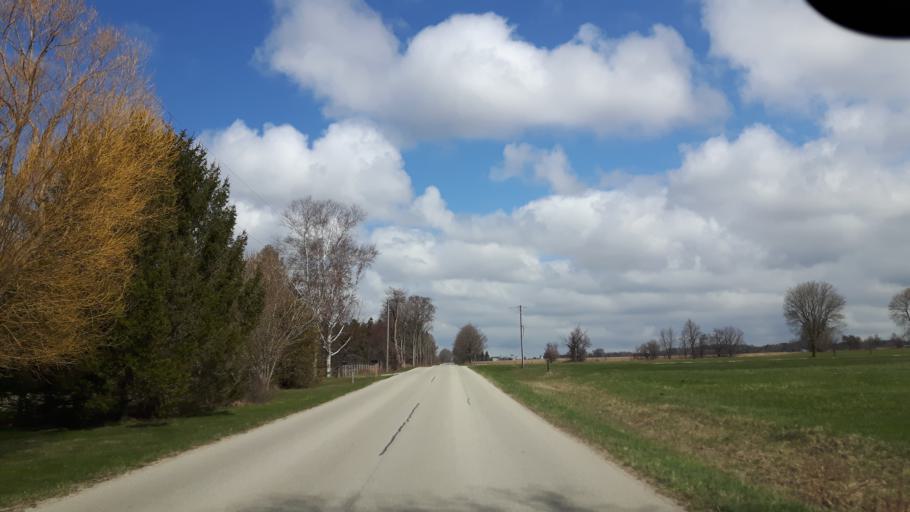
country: CA
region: Ontario
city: Goderich
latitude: 43.6292
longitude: -81.6846
